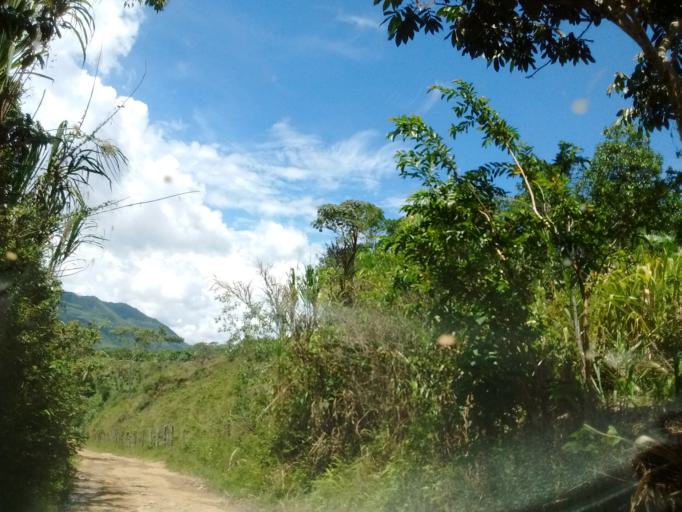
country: CO
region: Cauca
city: Villa Rica
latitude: 2.6454
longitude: -76.7712
